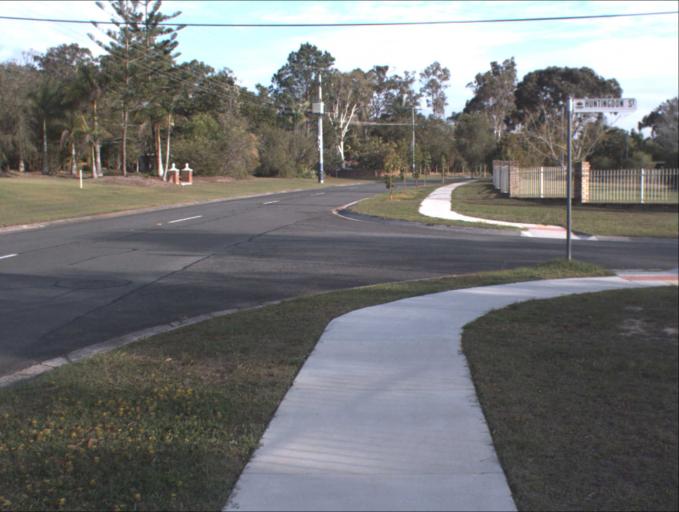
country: AU
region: Queensland
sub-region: Logan
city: Park Ridge South
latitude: -27.6746
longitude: 153.0138
